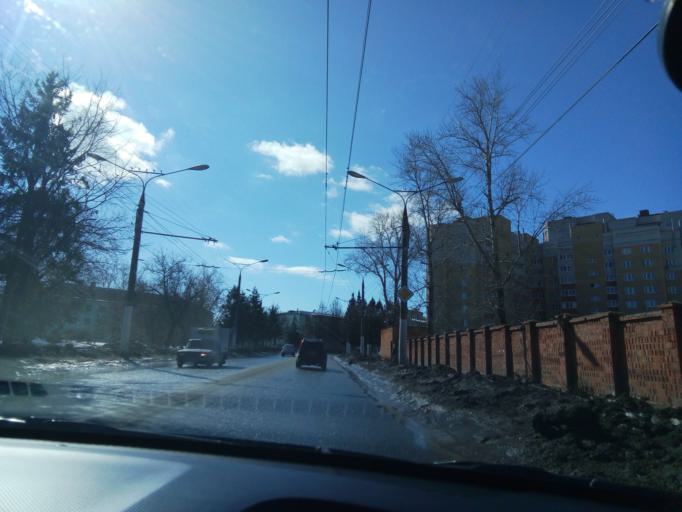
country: RU
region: Chuvashia
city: Novyye Lapsary
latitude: 56.1094
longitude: 47.1795
